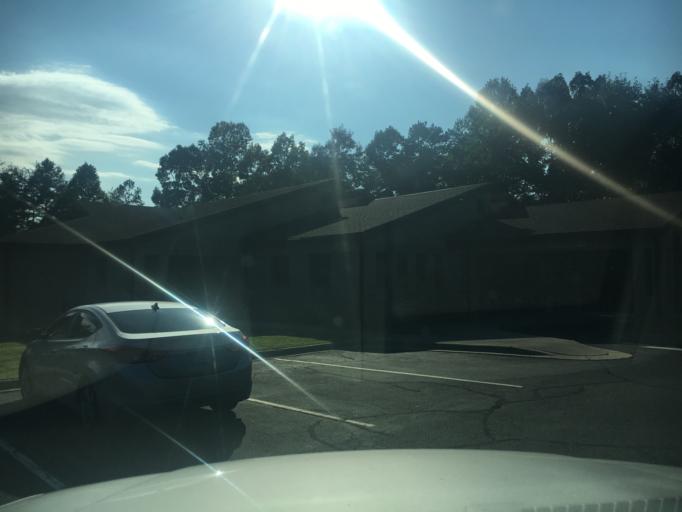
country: US
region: North Carolina
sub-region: McDowell County
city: West Marion
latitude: 35.6650
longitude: -82.0243
